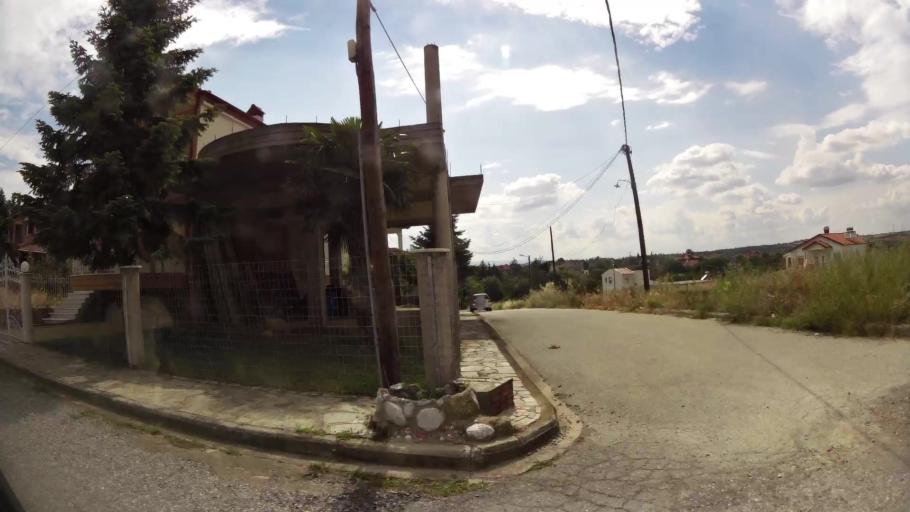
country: GR
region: Central Macedonia
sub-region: Nomos Pierias
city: Makrygialos
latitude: 40.4191
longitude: 22.6073
